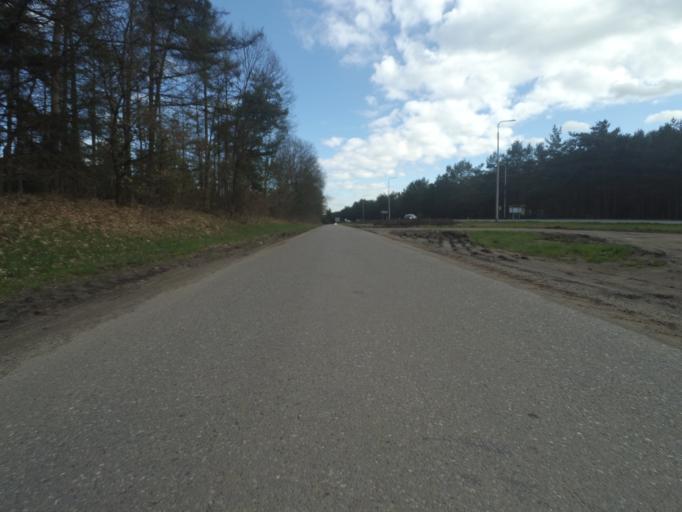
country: NL
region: Gelderland
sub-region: Gemeente Apeldoorn
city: Beekbergen
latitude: 52.1296
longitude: 5.9576
